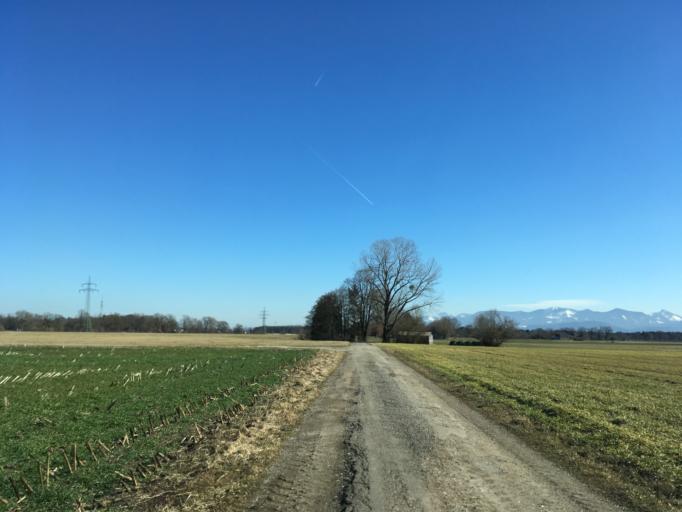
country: DE
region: Bavaria
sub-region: Upper Bavaria
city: Bad Aibling
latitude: 47.8436
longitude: 11.9950
